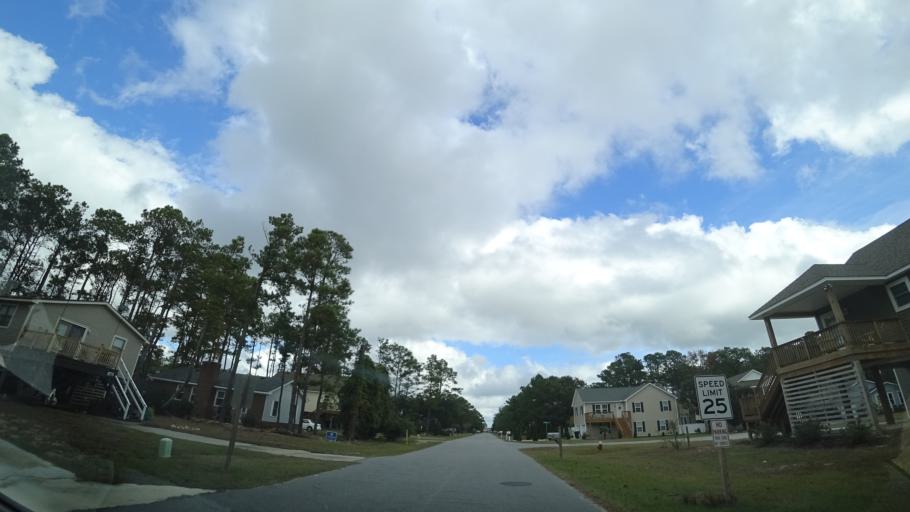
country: US
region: North Carolina
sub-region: Dare County
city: Kill Devil Hills
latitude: 35.9936
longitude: -75.6581
